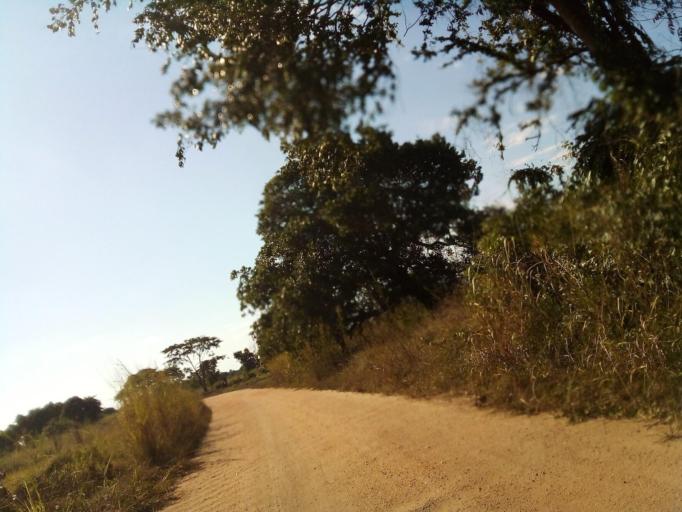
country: MZ
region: Zambezia
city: Quelimane
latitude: -17.5307
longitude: 36.6195
